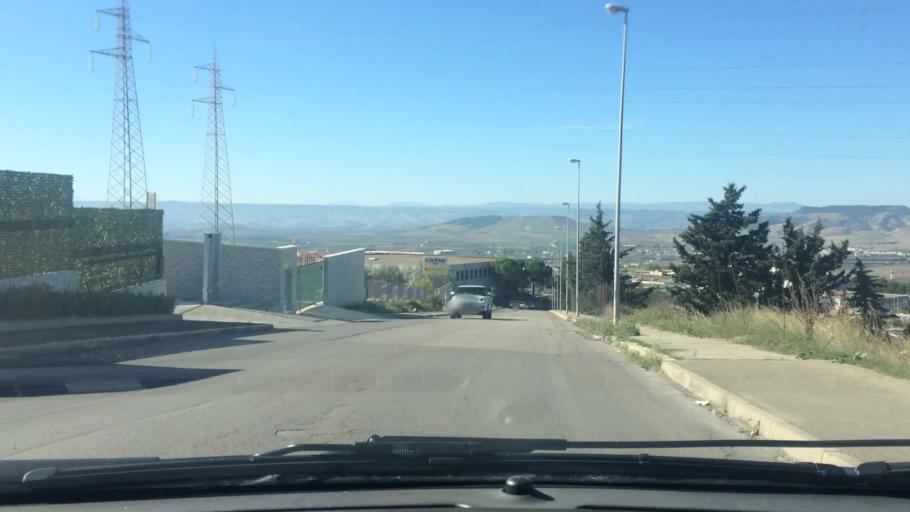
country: IT
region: Basilicate
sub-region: Provincia di Matera
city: Matera
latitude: 40.6750
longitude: 16.5759
